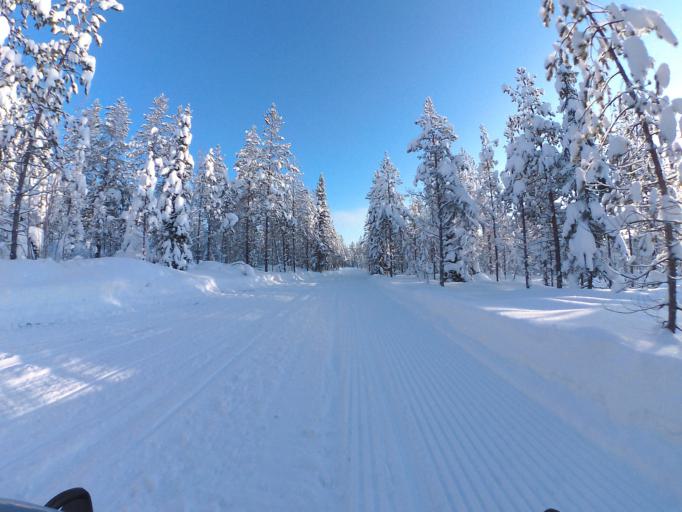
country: FI
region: Lapland
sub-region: Rovaniemi
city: Rovaniemi
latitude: 66.5984
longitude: 25.8413
